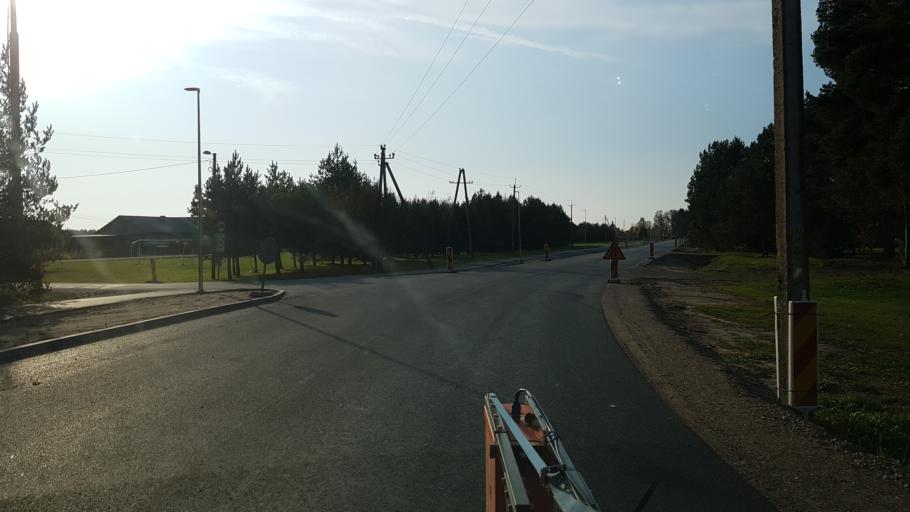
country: EE
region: Paernumaa
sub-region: Paikuse vald
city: Paikuse
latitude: 58.3471
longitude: 24.6220
